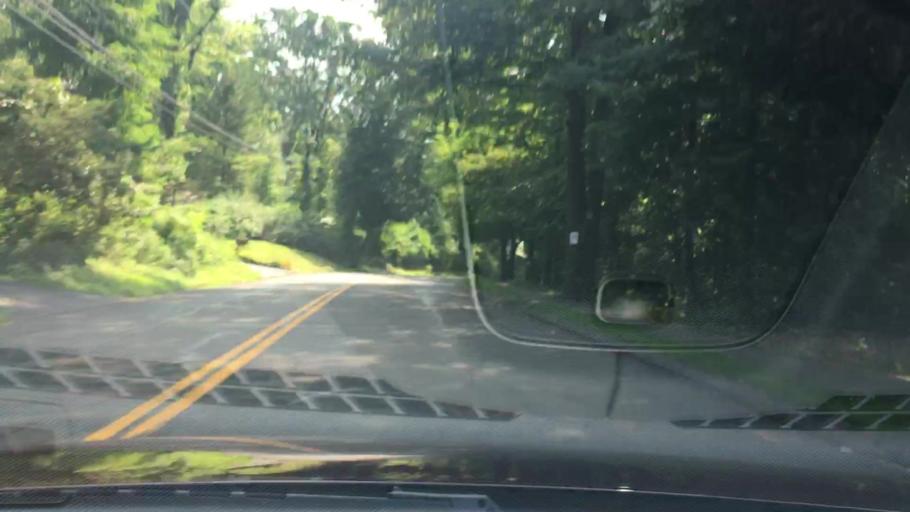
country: US
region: Connecticut
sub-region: Fairfield County
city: Norwalk
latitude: 41.1414
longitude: -73.4208
